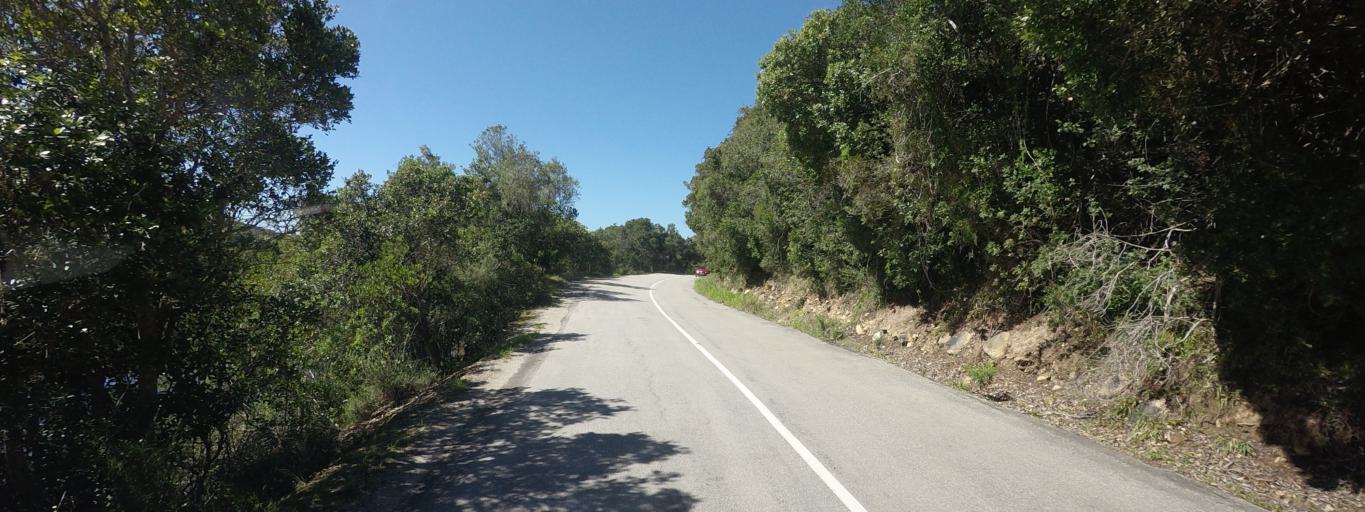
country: ZA
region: Western Cape
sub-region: Eden District Municipality
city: Plettenberg Bay
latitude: -33.9727
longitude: 23.5618
